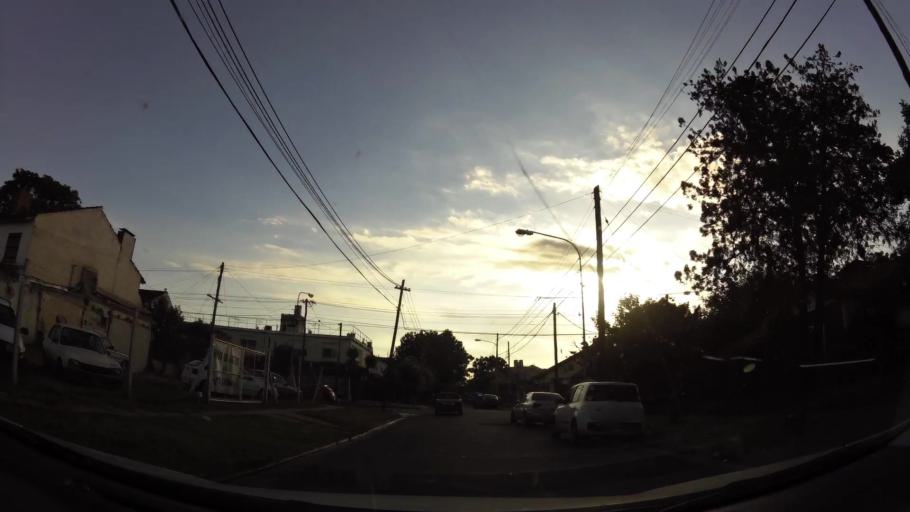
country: AR
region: Buenos Aires
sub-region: Partido de Tigre
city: Tigre
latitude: -34.4564
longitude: -58.6298
